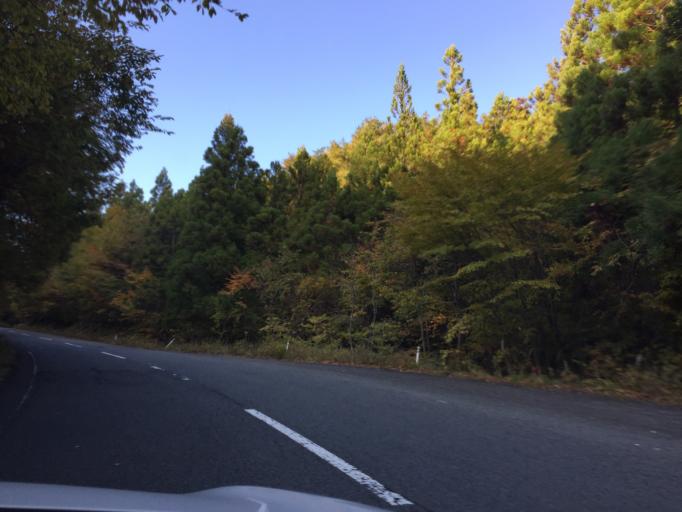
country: JP
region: Fukushima
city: Funehikimachi-funehiki
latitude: 37.2769
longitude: 140.7641
